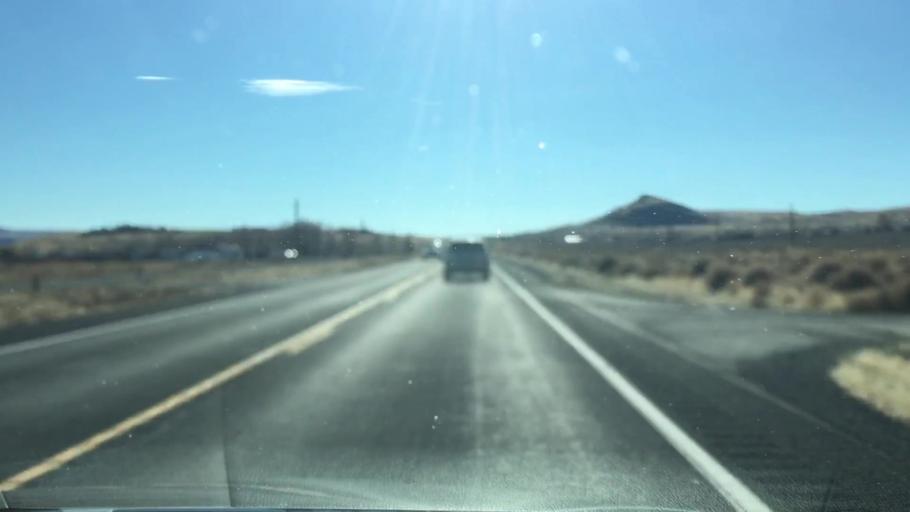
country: US
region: Nevada
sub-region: Lyon County
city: Silver Springs
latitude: 39.3515
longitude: -119.2387
